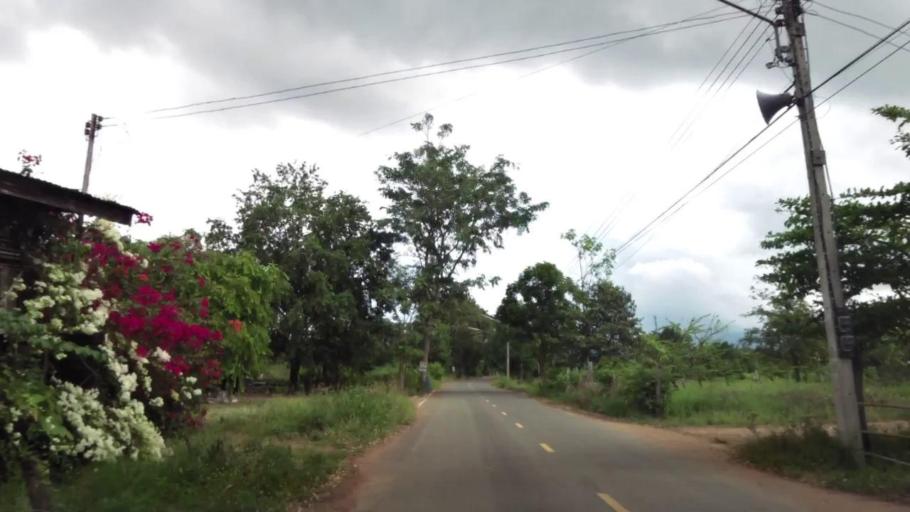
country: TH
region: Nakhon Sawan
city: Phai Sali
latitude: 15.6050
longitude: 100.6614
